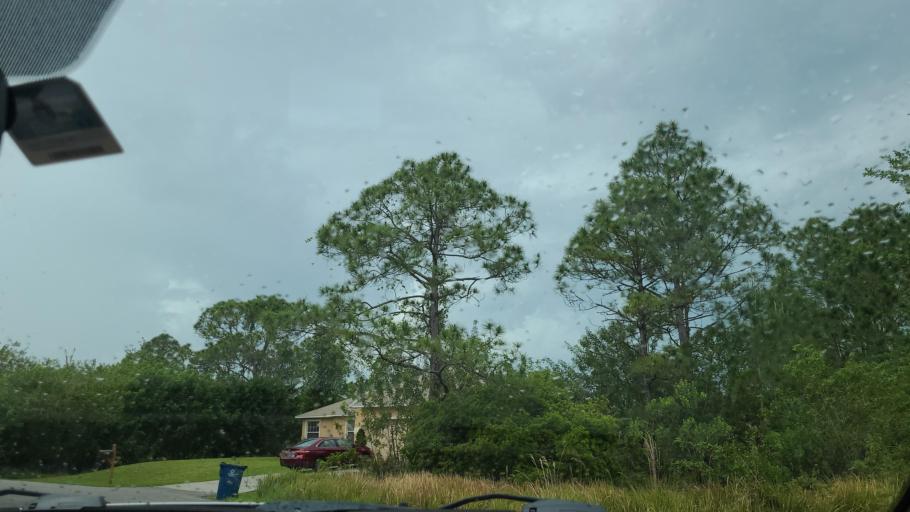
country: US
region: Florida
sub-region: Brevard County
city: Grant-Valkaria
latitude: 27.9495
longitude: -80.6378
